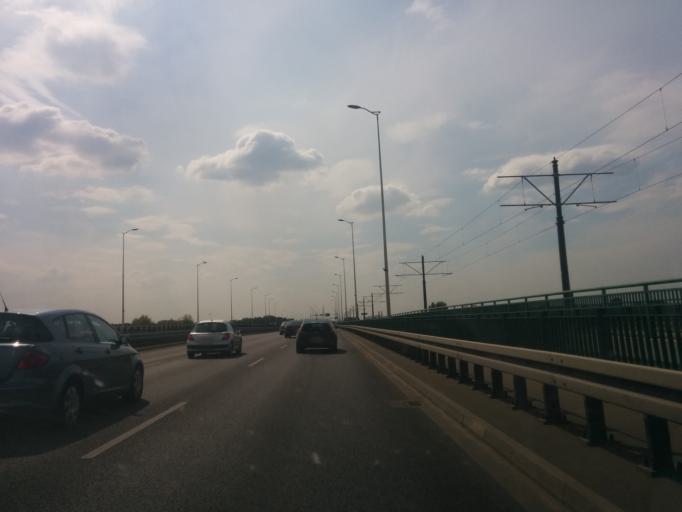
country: PL
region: Masovian Voivodeship
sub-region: Warszawa
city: Bielany
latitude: 52.3071
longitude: 20.9521
